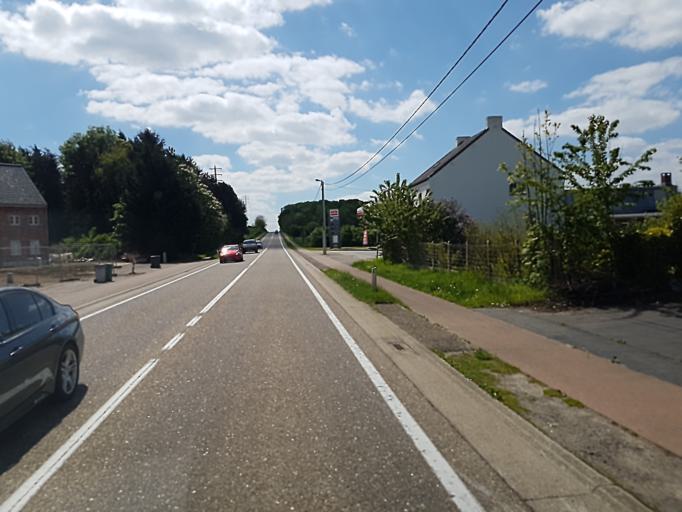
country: BE
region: Flanders
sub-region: Provincie Vlaams-Brabant
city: Bekkevoort
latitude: 50.9150
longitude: 4.9802
